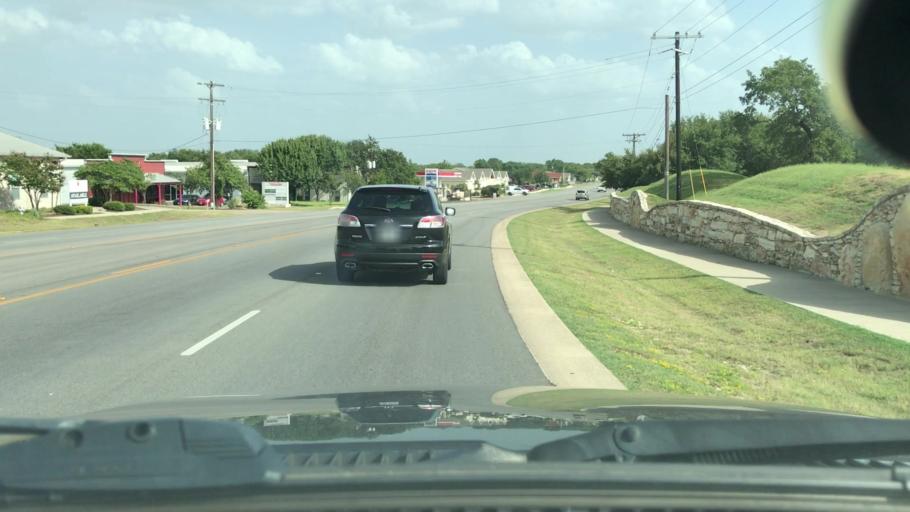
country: US
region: Texas
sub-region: Williamson County
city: Leander
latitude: 30.5504
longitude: -97.8541
